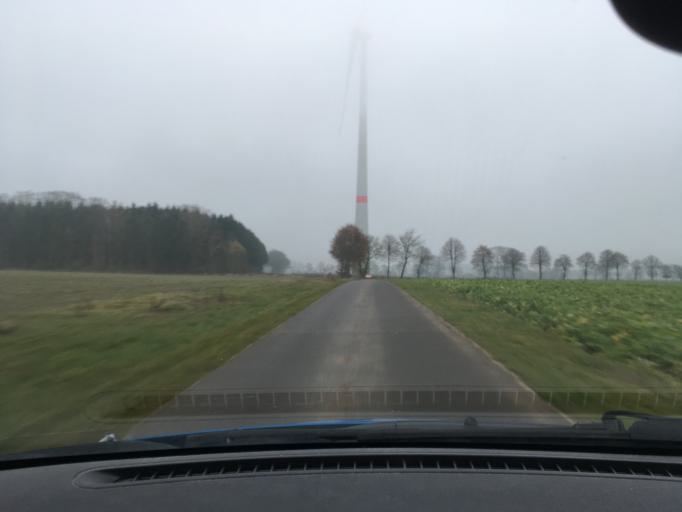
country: DE
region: Lower Saxony
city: Amelinghausen
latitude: 53.1082
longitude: 10.1938
